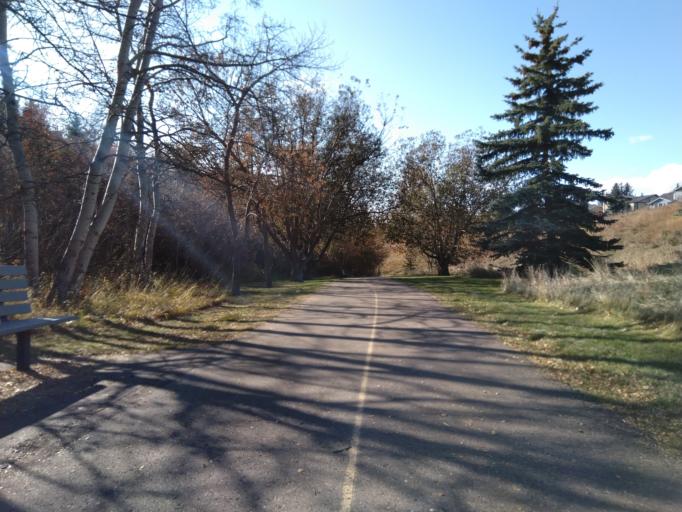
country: CA
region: Alberta
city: Calgary
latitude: 51.1346
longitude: -114.1500
